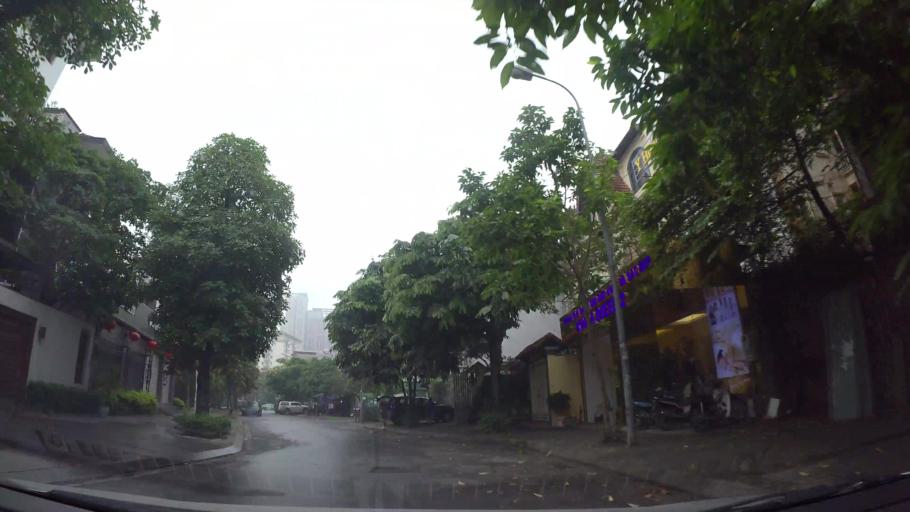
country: VN
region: Ha Noi
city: Cau Giay
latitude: 21.0192
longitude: 105.7957
